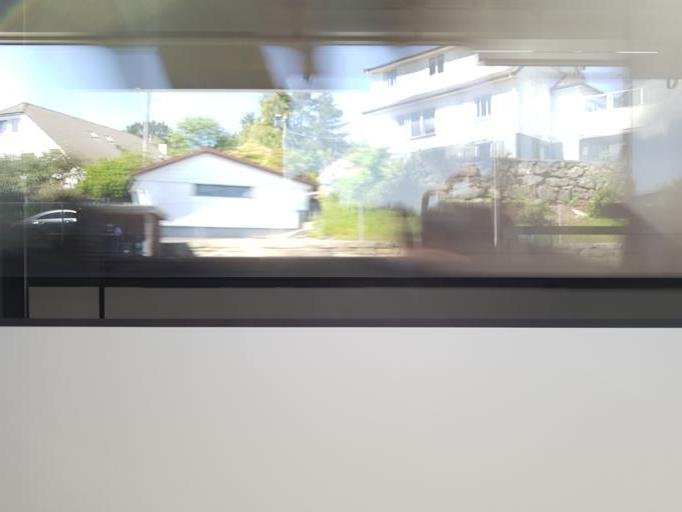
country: NO
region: Hordaland
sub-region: Bergen
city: Ytrebygda
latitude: 60.2905
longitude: 5.2649
